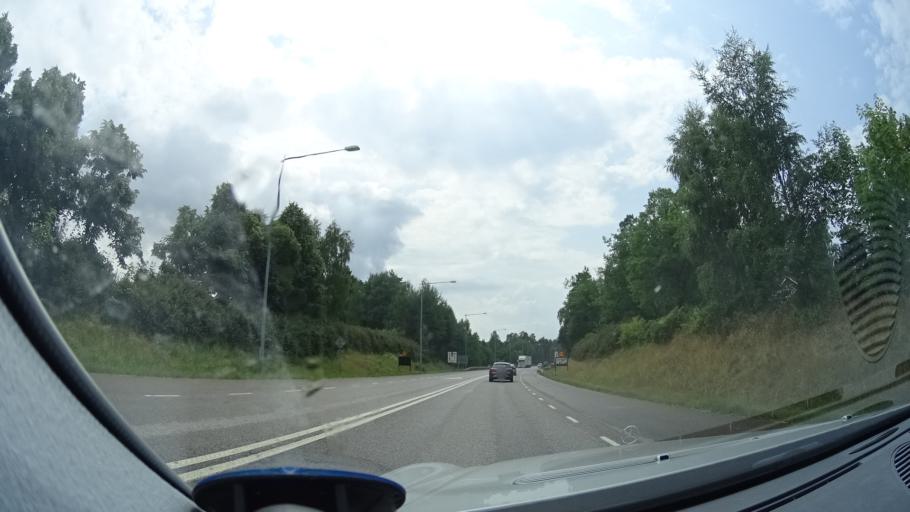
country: SE
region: Kalmar
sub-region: Nybro Kommun
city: Nybro
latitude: 56.7329
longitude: 15.9317
